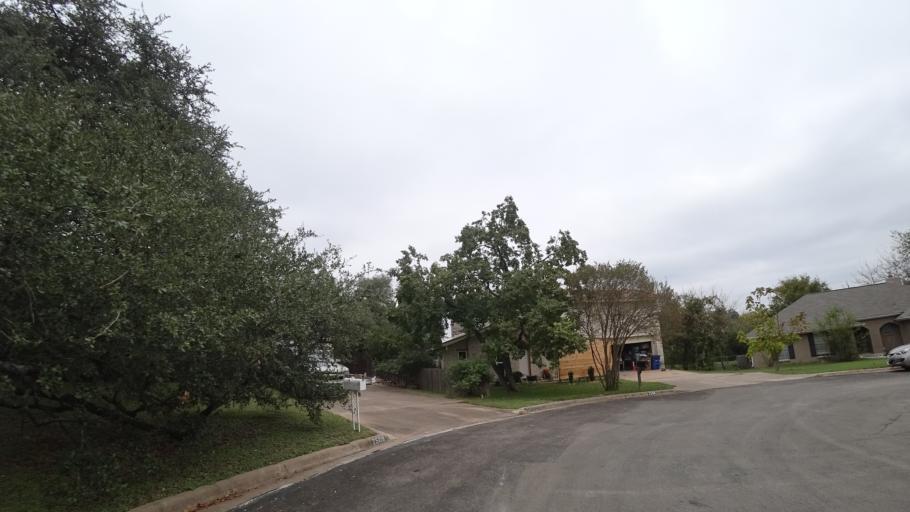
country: US
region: Texas
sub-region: Travis County
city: Barton Creek
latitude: 30.2396
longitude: -97.8819
